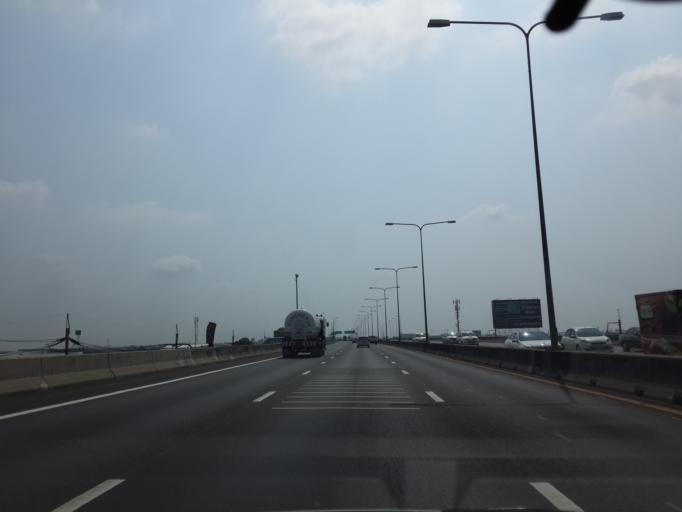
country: TH
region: Samut Prakan
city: Bang Bo District
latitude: 13.6111
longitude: 100.7598
